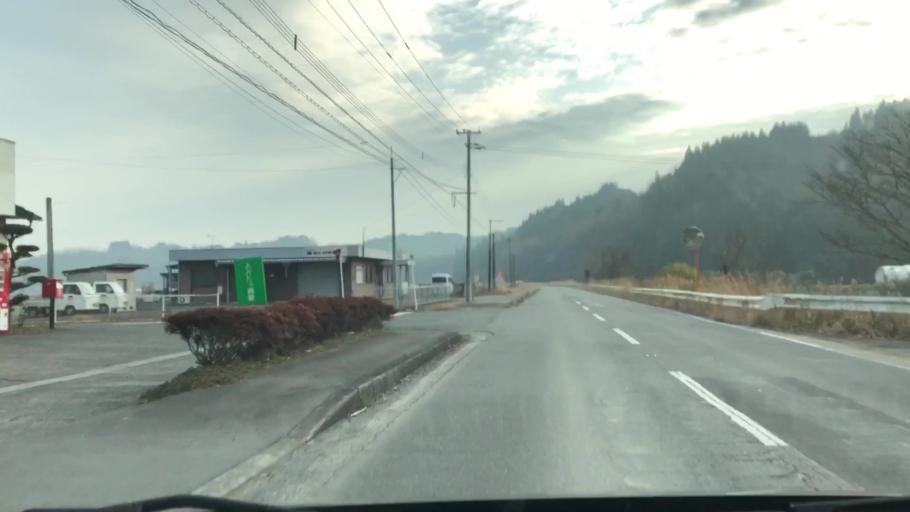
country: JP
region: Oita
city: Takedamachi
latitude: 32.9643
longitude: 131.4879
